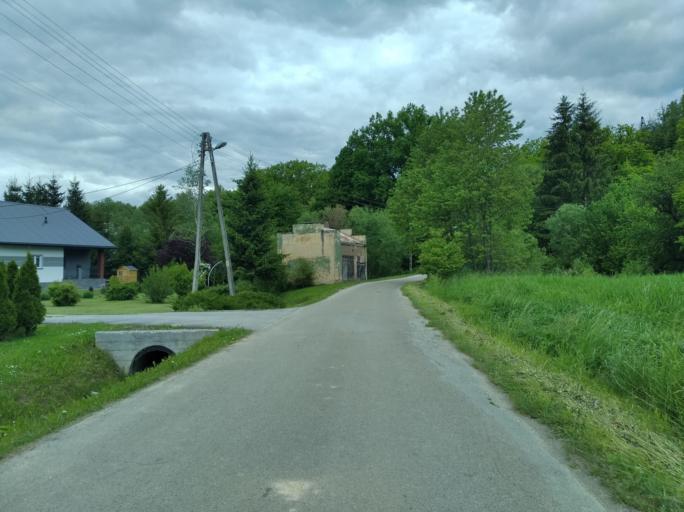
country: PL
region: Subcarpathian Voivodeship
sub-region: Powiat brzozowski
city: Jasionow
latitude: 49.6675
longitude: 21.9882
